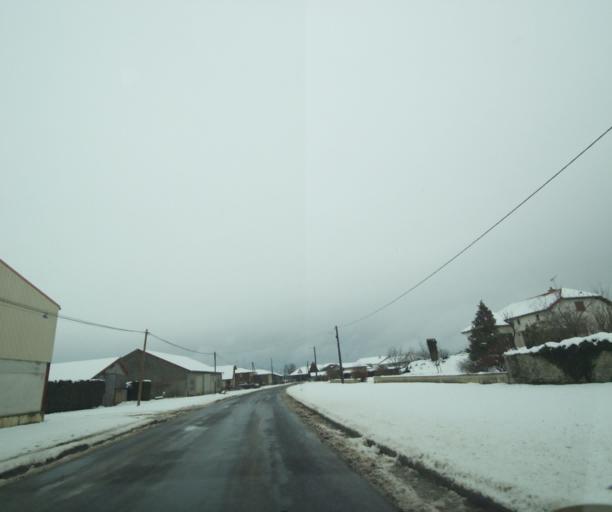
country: FR
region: Champagne-Ardenne
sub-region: Departement de la Haute-Marne
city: Montier-en-Der
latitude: 48.4399
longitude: 4.8024
